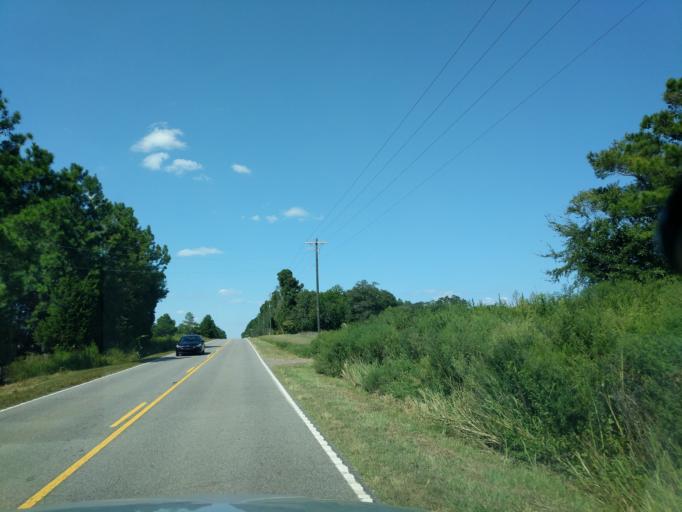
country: US
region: South Carolina
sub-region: Lexington County
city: Leesville
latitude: 33.9695
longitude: -81.5287
